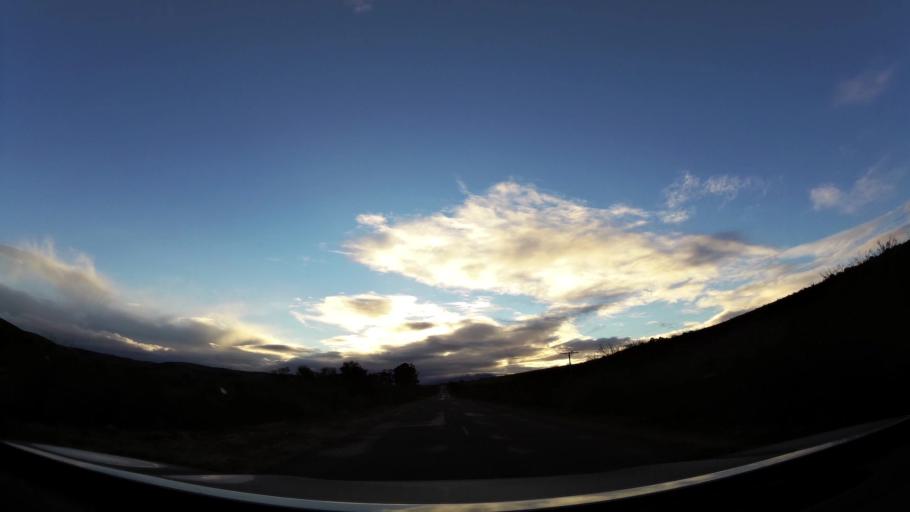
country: ZA
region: Western Cape
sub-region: Eden District Municipality
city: Riversdale
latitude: -34.0657
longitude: 20.8929
